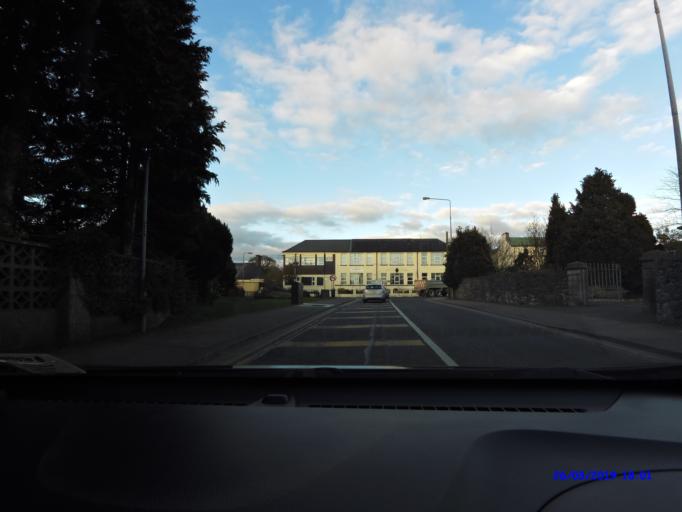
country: IE
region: Connaught
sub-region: County Galway
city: Tuam
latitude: 53.5119
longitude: -8.8481
